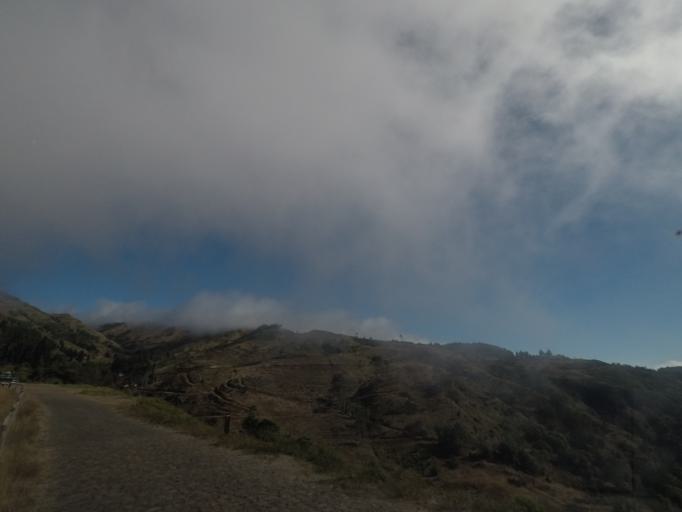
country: PT
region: Madeira
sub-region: Funchal
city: Nossa Senhora do Monte
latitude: 32.6943
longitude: -16.9038
